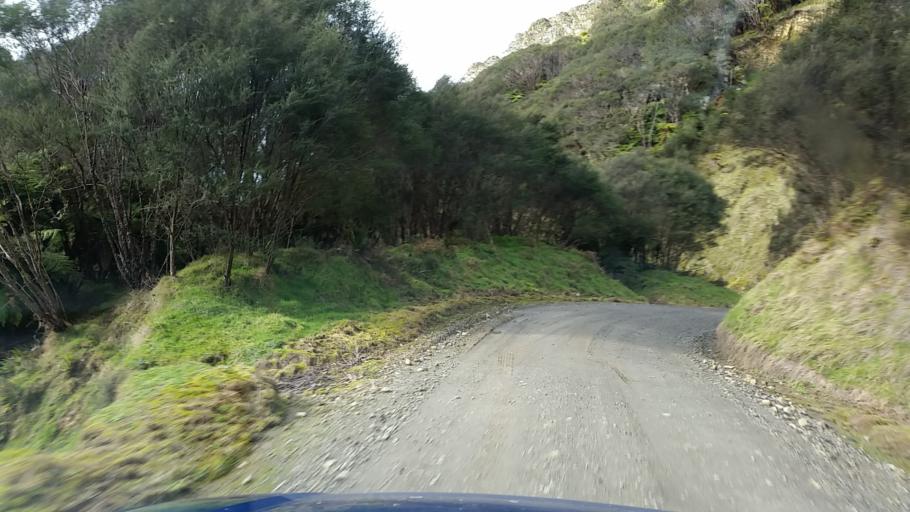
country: NZ
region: Taranaki
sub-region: South Taranaki District
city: Eltham
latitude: -39.2660
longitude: 174.7715
